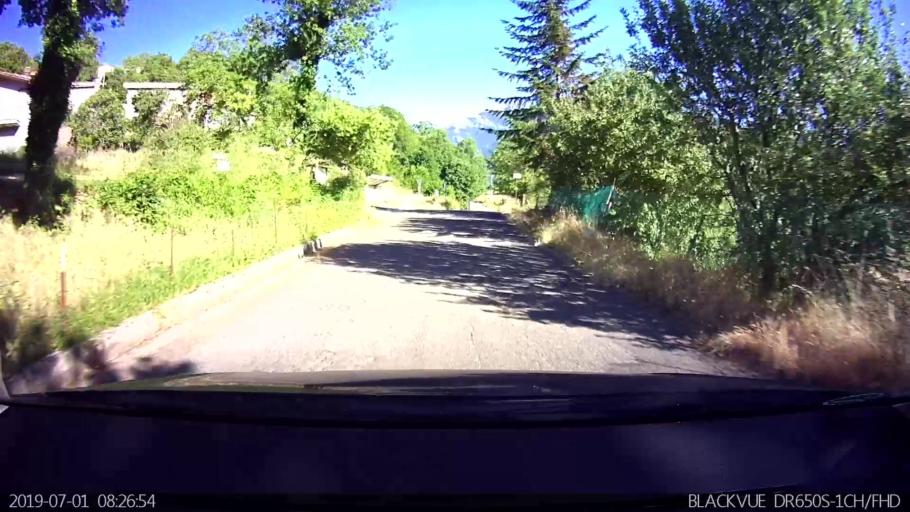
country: IT
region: Latium
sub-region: Provincia di Frosinone
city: Collepardo
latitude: 41.7714
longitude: 13.4045
